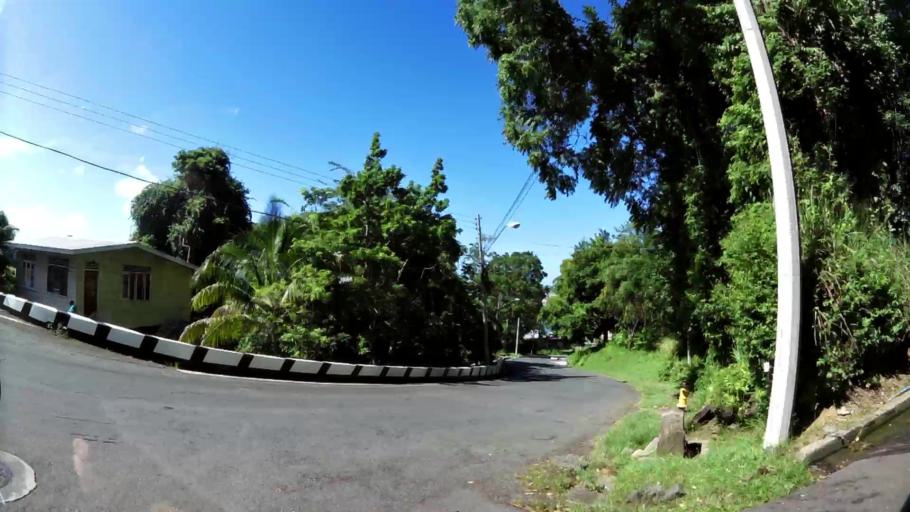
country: TT
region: Tobago
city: Scarborough
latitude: 11.1812
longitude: -60.7311
